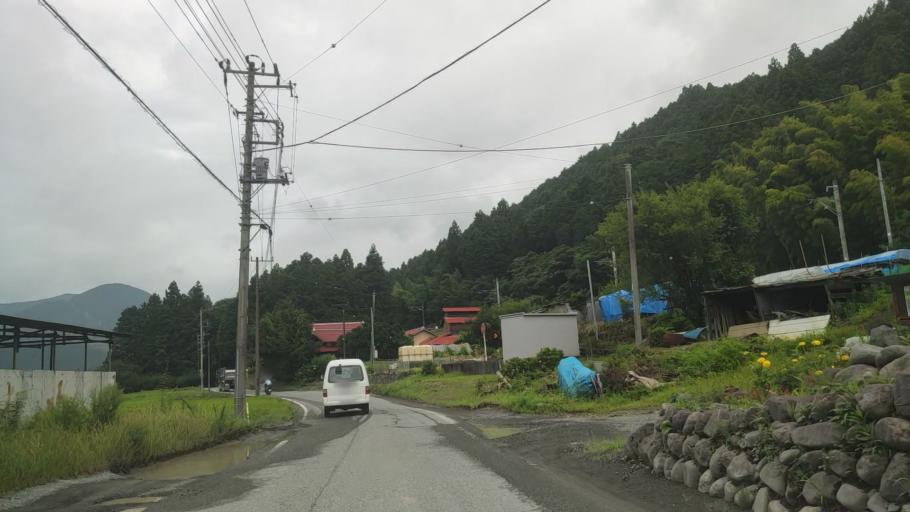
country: JP
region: Shizuoka
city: Fujinomiya
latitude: 35.2178
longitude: 138.5434
